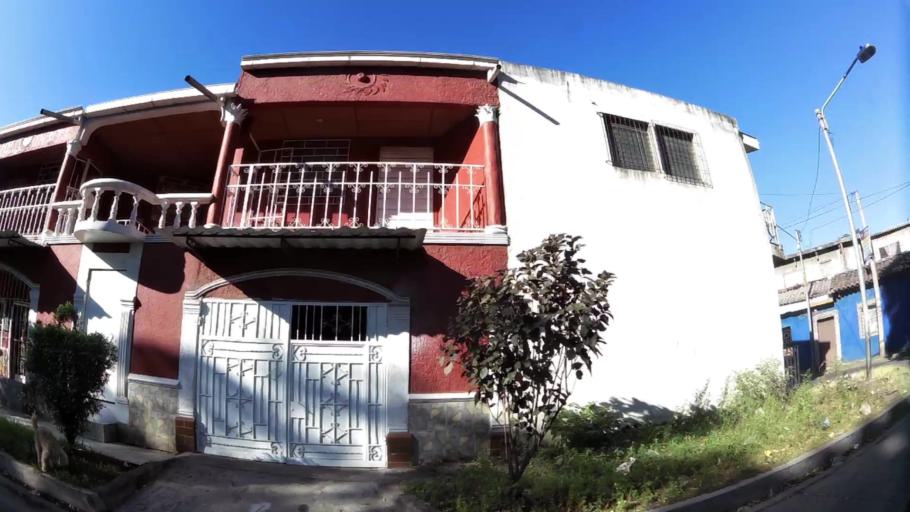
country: SV
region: Sonsonate
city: Sonsonate
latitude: 13.7147
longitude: -89.7184
